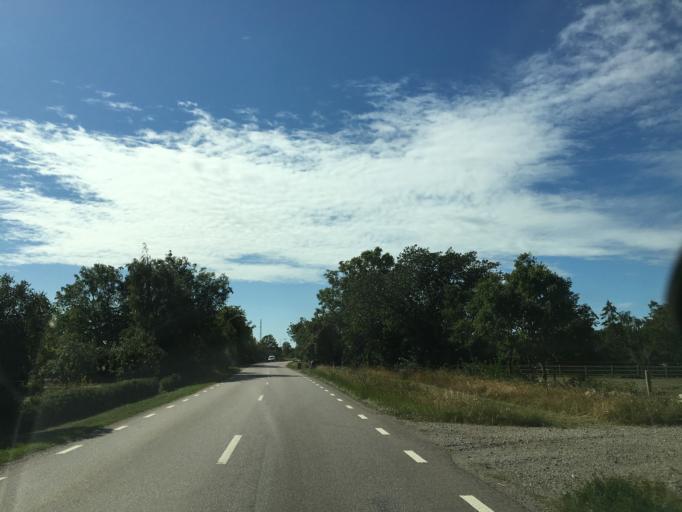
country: SE
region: Kalmar
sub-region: Morbylanga Kommun
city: Moerbylanga
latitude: 56.5237
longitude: 16.4403
